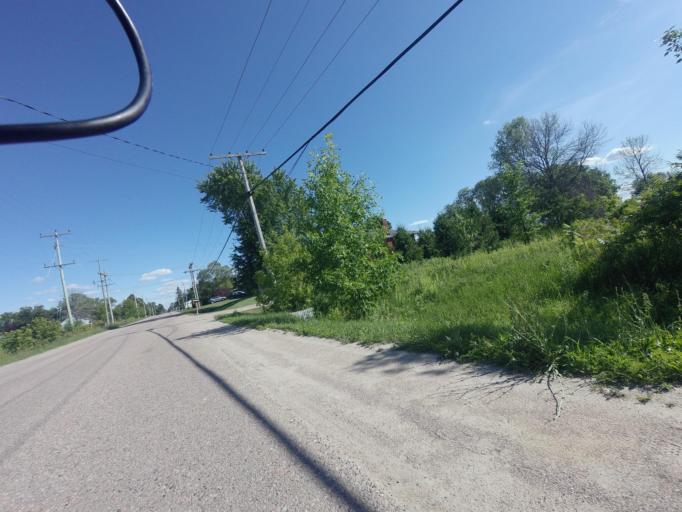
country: CA
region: Ontario
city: Arnprior
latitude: 45.4202
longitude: -76.3867
